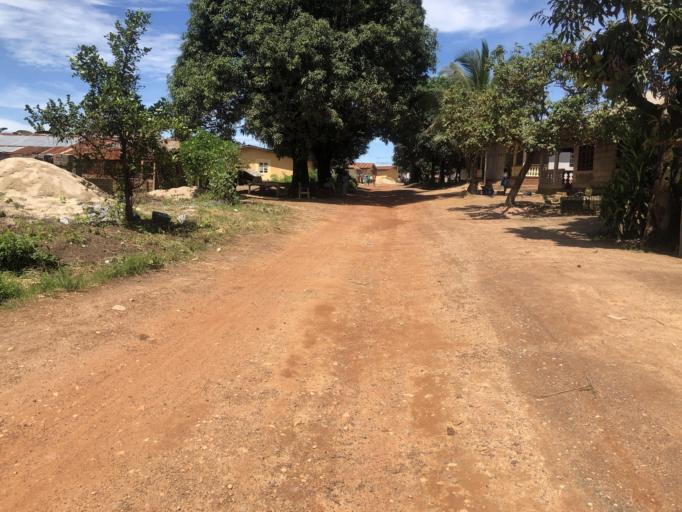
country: SL
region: Eastern Province
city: Koidu
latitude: 8.6416
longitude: -10.9652
